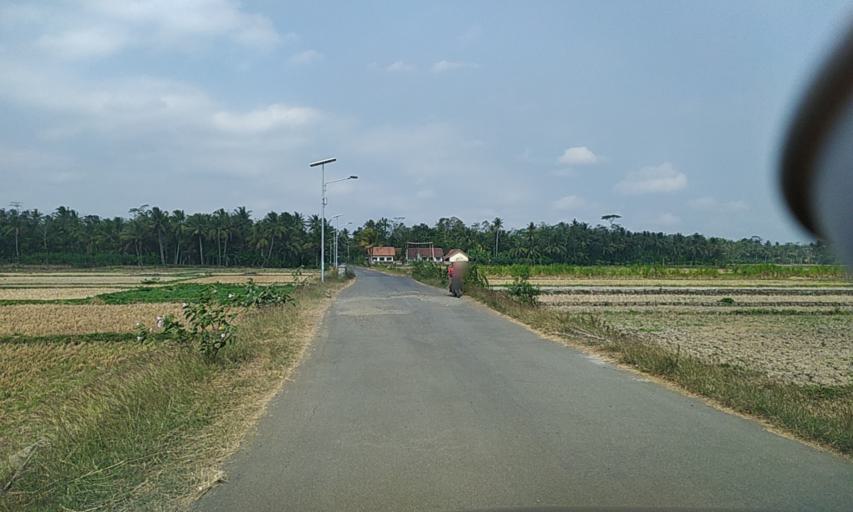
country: ID
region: Central Java
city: Kemantren Satu
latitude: -7.5259
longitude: 108.8767
